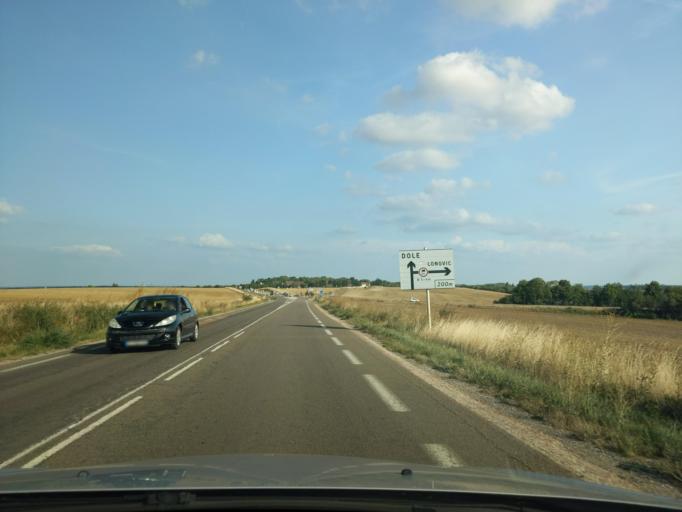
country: FR
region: Bourgogne
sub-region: Departement de la Cote-d'Or
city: Sennecey-les-Dijon
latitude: 47.2934
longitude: 5.0885
